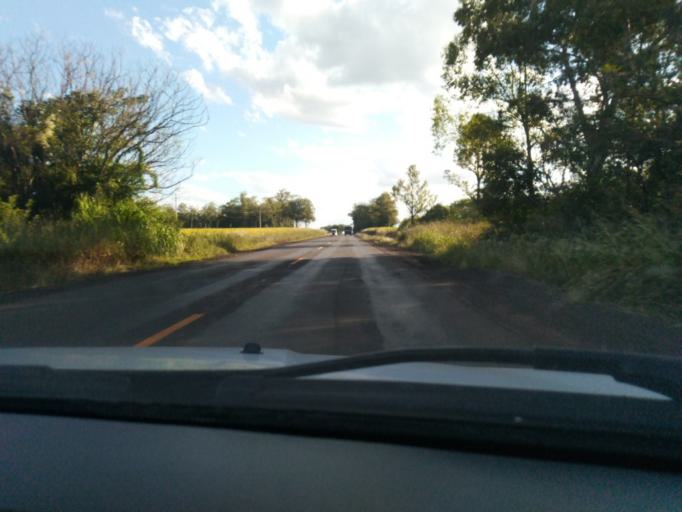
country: AR
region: Corrientes
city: Garruchos
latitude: -28.5482
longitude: -55.5618
